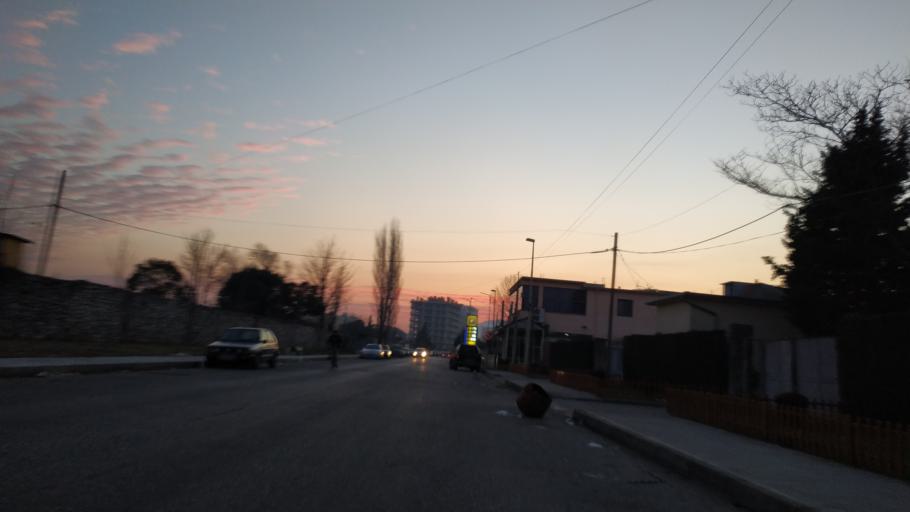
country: AL
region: Shkoder
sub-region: Rrethi i Shkodres
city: Shkoder
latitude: 42.0804
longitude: 19.5244
